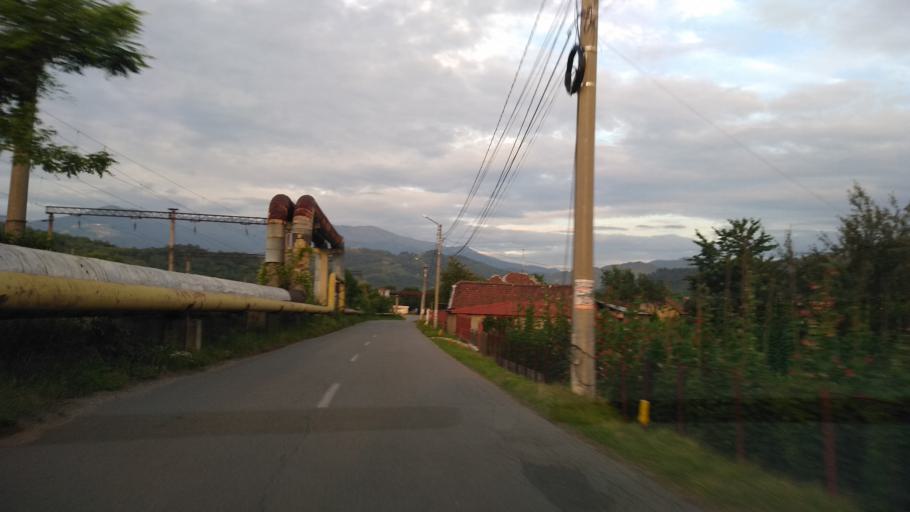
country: RO
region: Hunedoara
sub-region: Comuna Aninoasa
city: Iscroni
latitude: 45.3794
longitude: 23.3308
